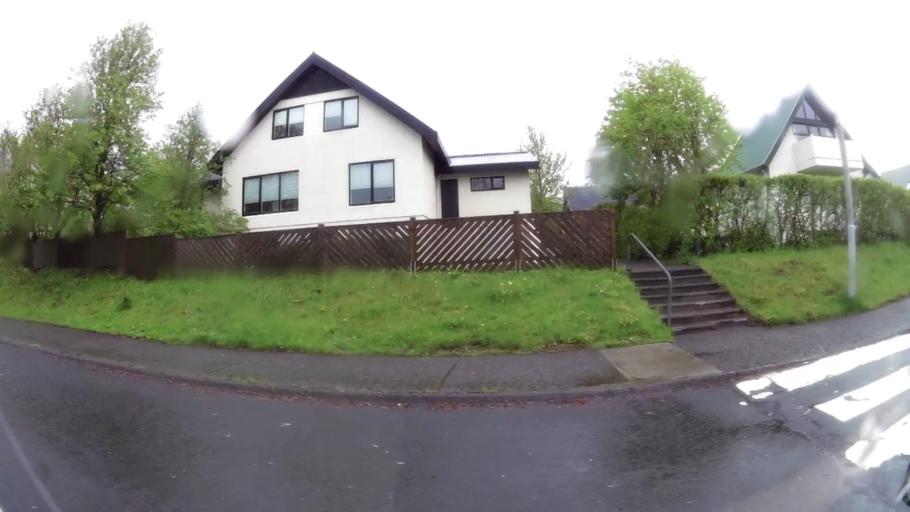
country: IS
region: Capital Region
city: Reykjavik
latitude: 64.0951
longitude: -21.8453
